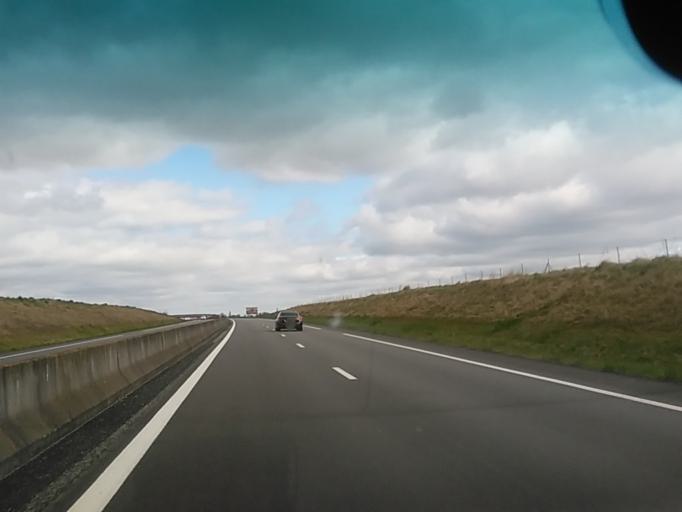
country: FR
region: Haute-Normandie
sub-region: Departement de l'Eure
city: Thiberville
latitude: 49.0974
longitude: 0.5011
